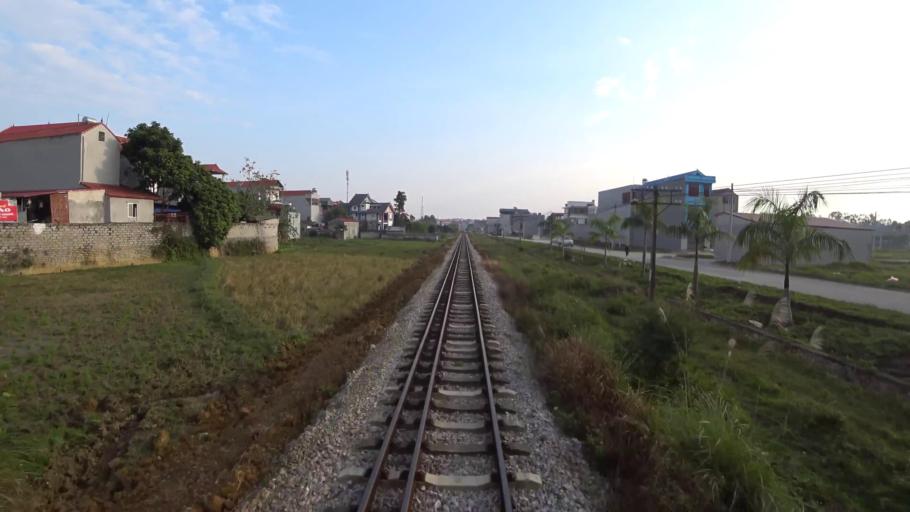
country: VN
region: Lang Son
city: Thi Tran Cao Loc
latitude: 21.8814
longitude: 106.7492
